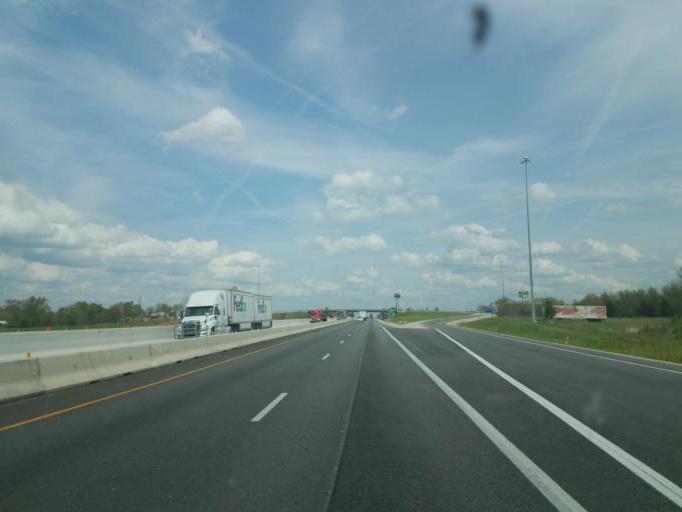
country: US
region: Kentucky
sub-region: Larue County
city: Hodgenville
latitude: 37.5177
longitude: -85.8856
